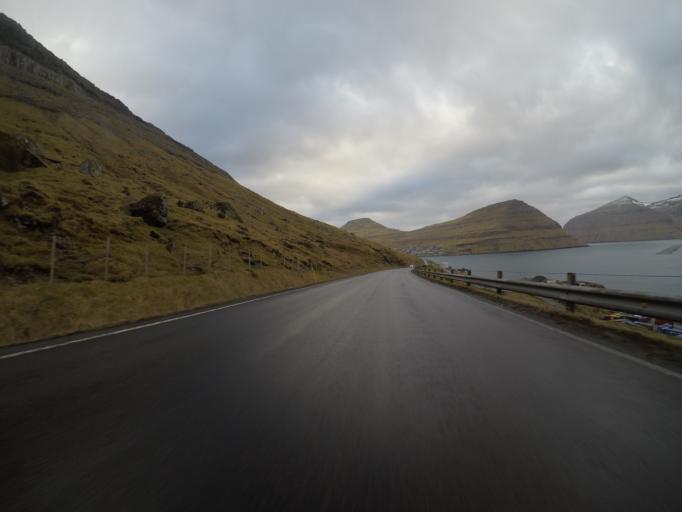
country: FO
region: Nordoyar
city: Klaksvik
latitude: 62.2519
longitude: -6.5783
